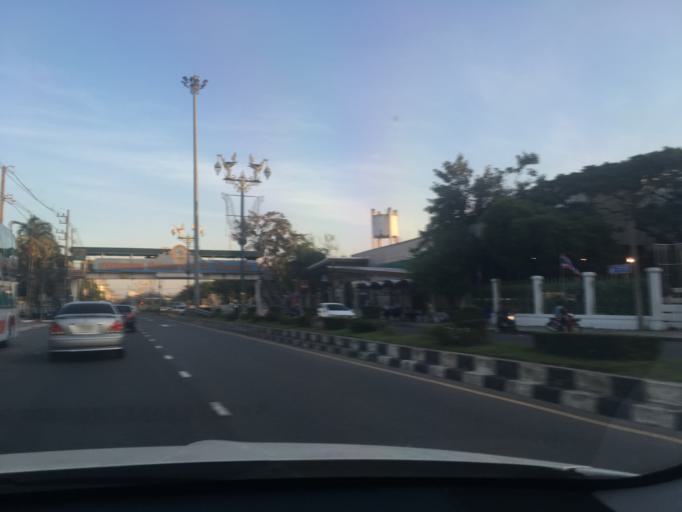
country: TH
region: Chon Buri
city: Ban Bueng
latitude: 13.3137
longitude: 101.1104
